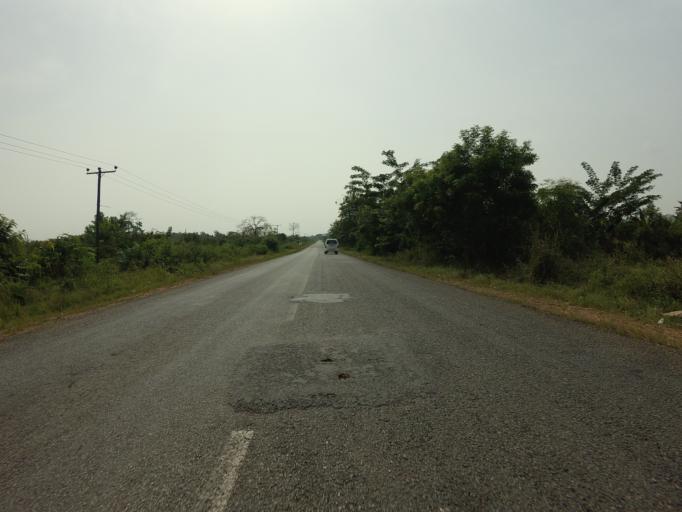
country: GH
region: Volta
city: Ho
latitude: 6.3956
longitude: 0.1800
